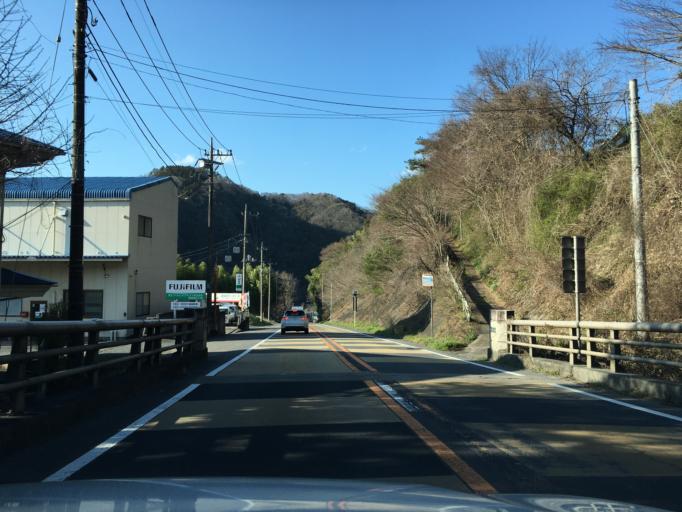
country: JP
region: Ibaraki
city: Daigo
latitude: 36.6786
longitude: 140.3892
